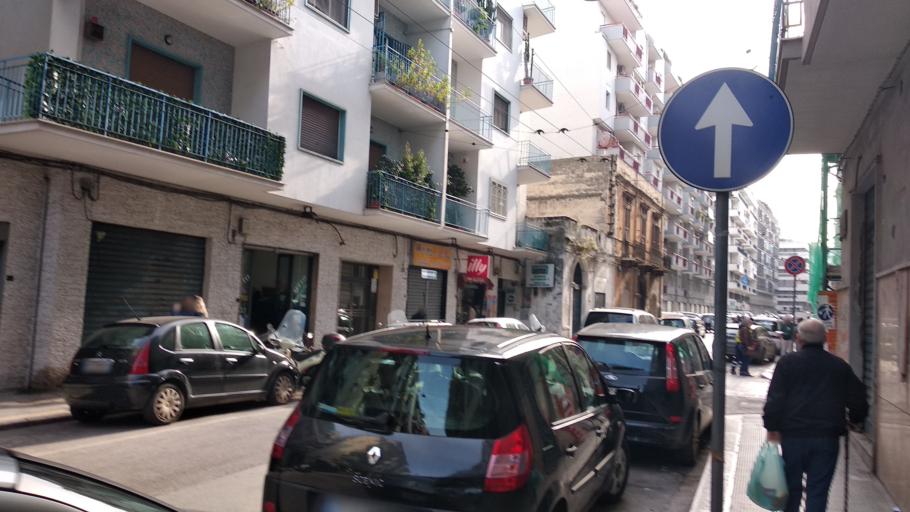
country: IT
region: Apulia
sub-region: Provincia di Bari
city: Bari
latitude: 41.1163
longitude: 16.8779
